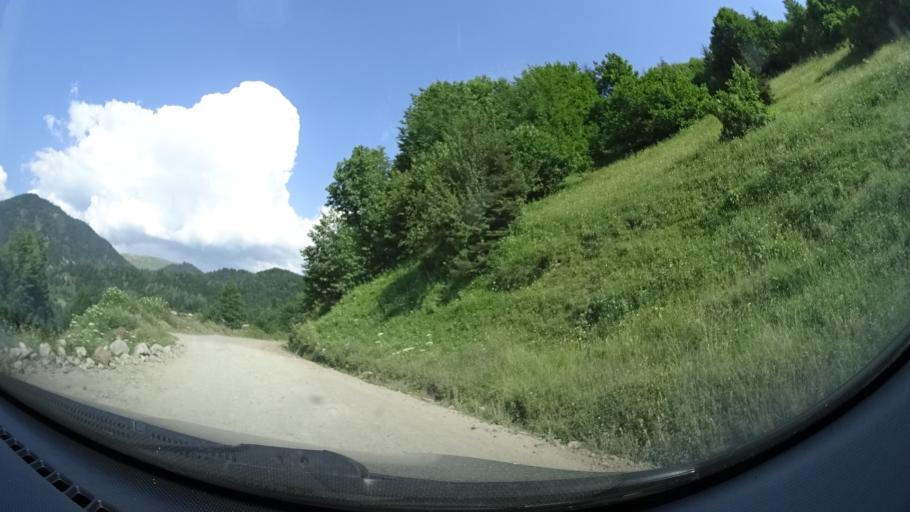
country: GE
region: Ajaria
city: Dioknisi
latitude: 41.6521
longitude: 42.4617
